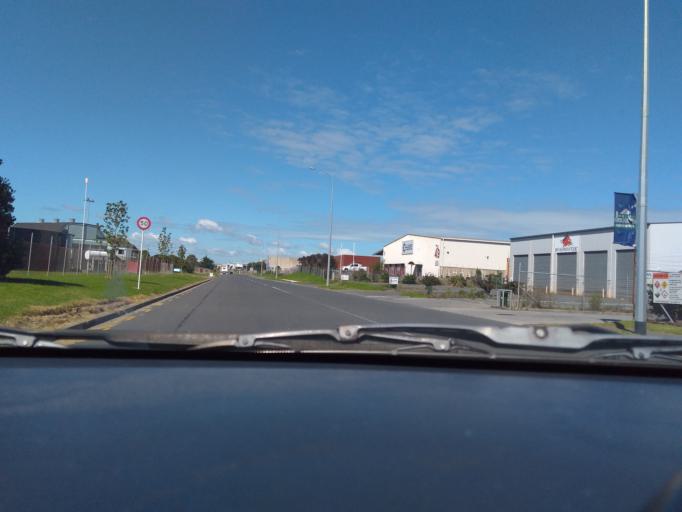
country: NZ
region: Auckland
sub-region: Auckland
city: Wiri
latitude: -37.0032
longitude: 174.8488
